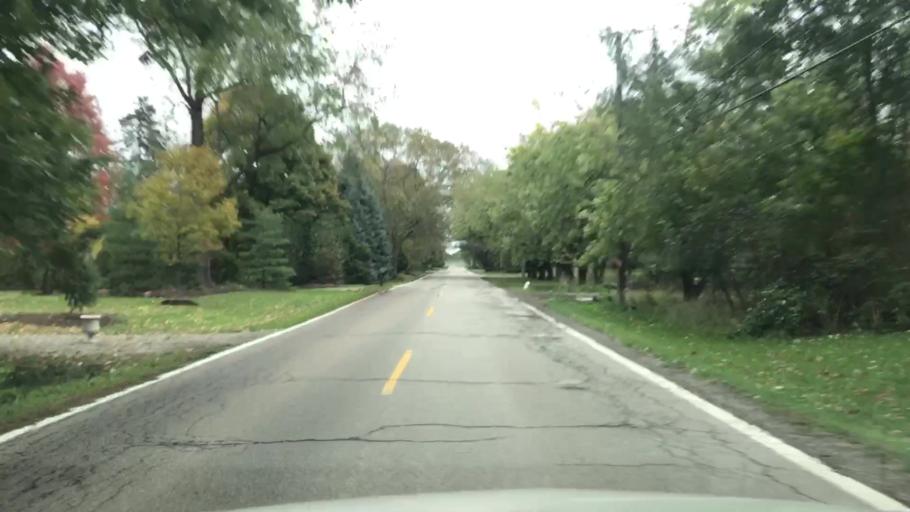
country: US
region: Michigan
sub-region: Oakland County
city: Rochester
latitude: 42.7417
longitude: -83.0820
